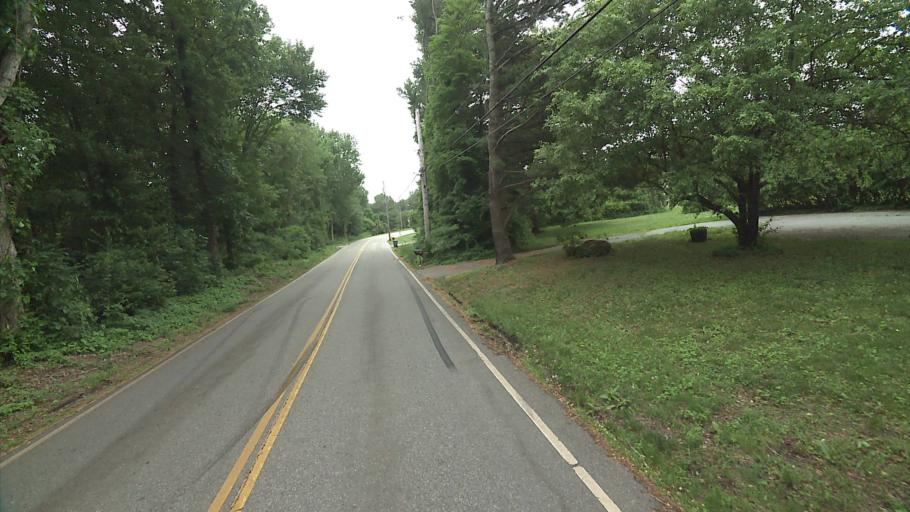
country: US
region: Connecticut
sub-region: Tolland County
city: Hebron
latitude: 41.6722
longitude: -72.3564
